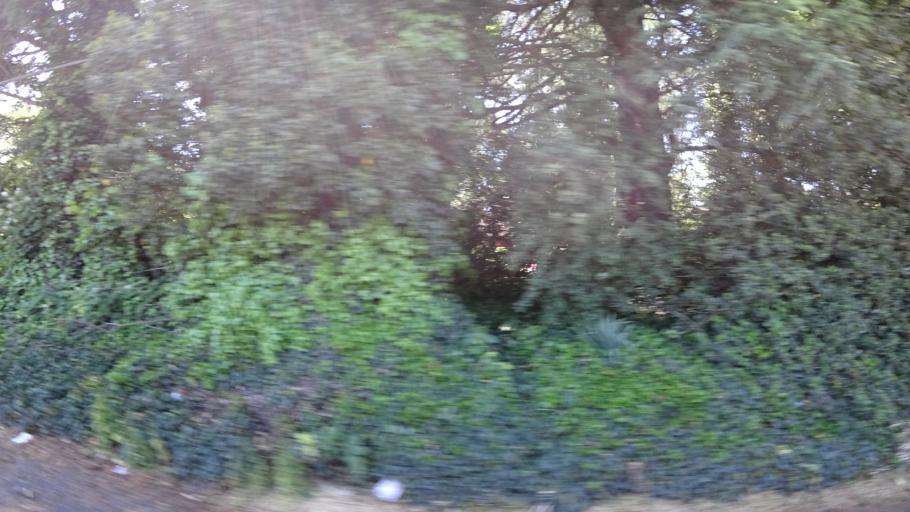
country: US
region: Oregon
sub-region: Multnomah County
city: Gresham
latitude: 45.4889
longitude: -122.4847
